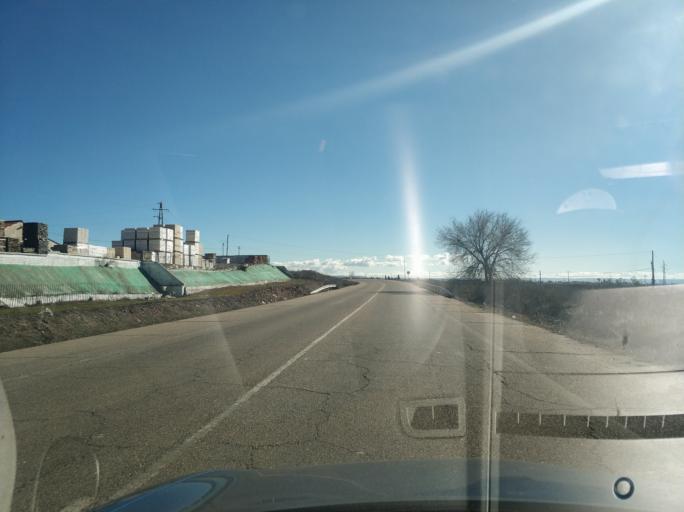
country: ES
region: Castille and Leon
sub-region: Provincia de Valladolid
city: Cisterniga
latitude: 41.6044
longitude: -4.6779
